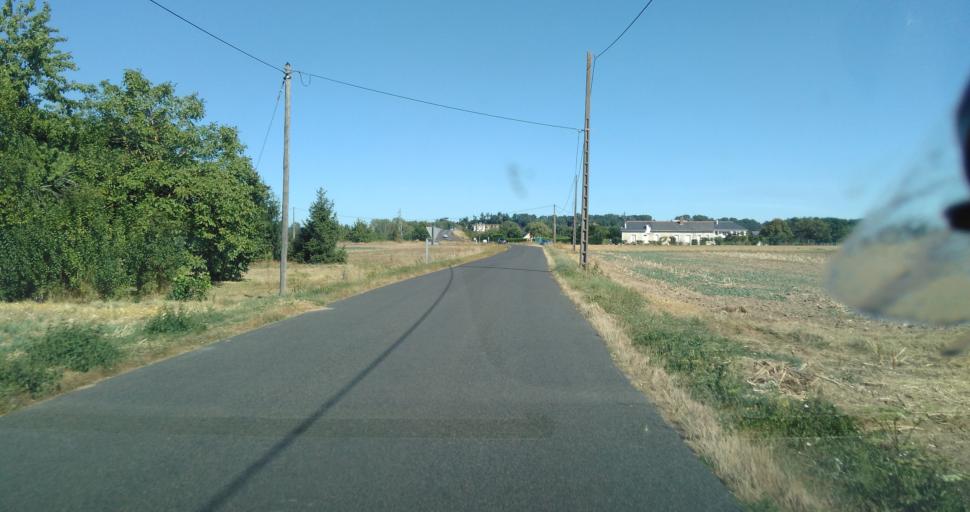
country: FR
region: Centre
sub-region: Departement d'Indre-et-Loire
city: Vernou-sur-Brenne
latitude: 47.4011
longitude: 0.8555
